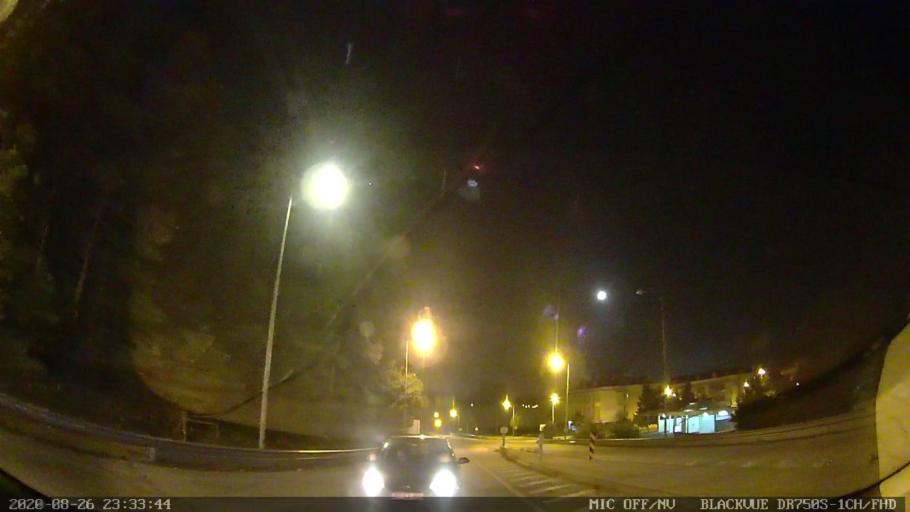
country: PT
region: Viseu
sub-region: Viseu
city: Rio de Loba
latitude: 40.6795
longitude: -7.8833
